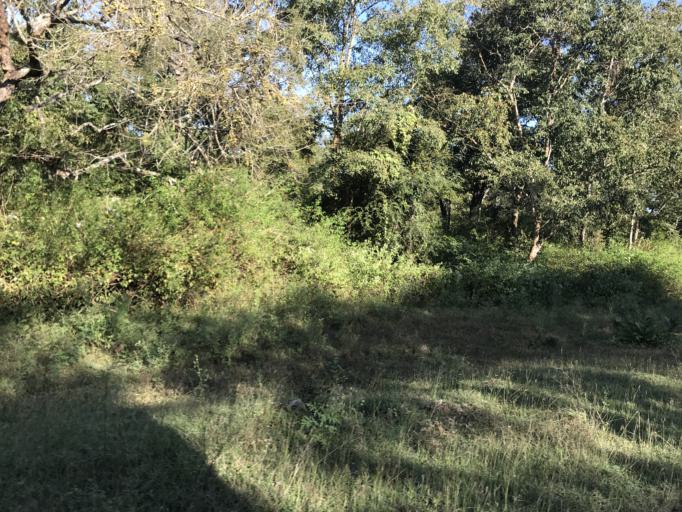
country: IN
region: Karnataka
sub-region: Mysore
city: Heggadadevankote
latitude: 11.9703
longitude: 76.2444
